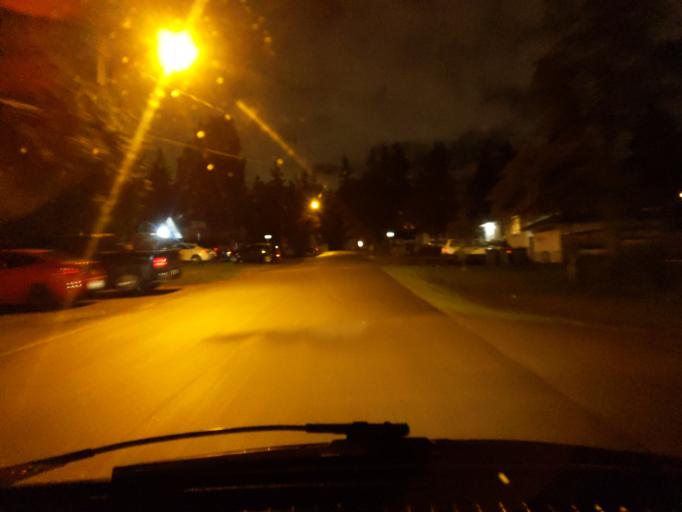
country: CA
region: British Columbia
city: New Westminster
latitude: 49.1968
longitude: -122.8646
